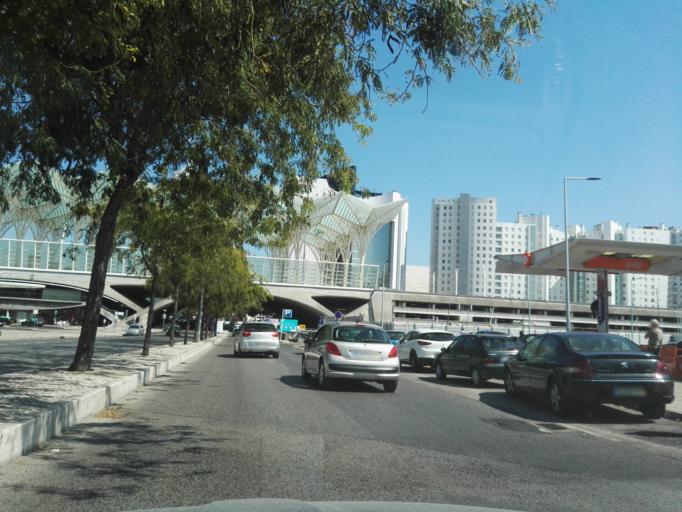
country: PT
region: Lisbon
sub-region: Loures
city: Moscavide
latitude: 38.7672
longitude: -9.1011
